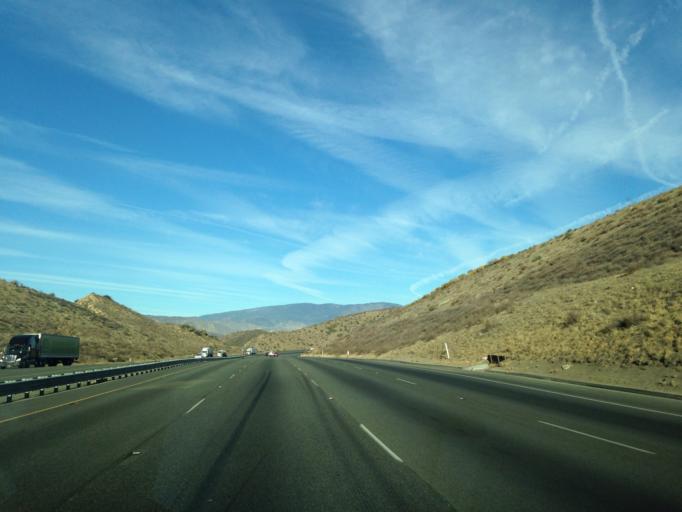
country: US
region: California
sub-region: Los Angeles County
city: Castaic
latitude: 34.6375
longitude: -118.7438
